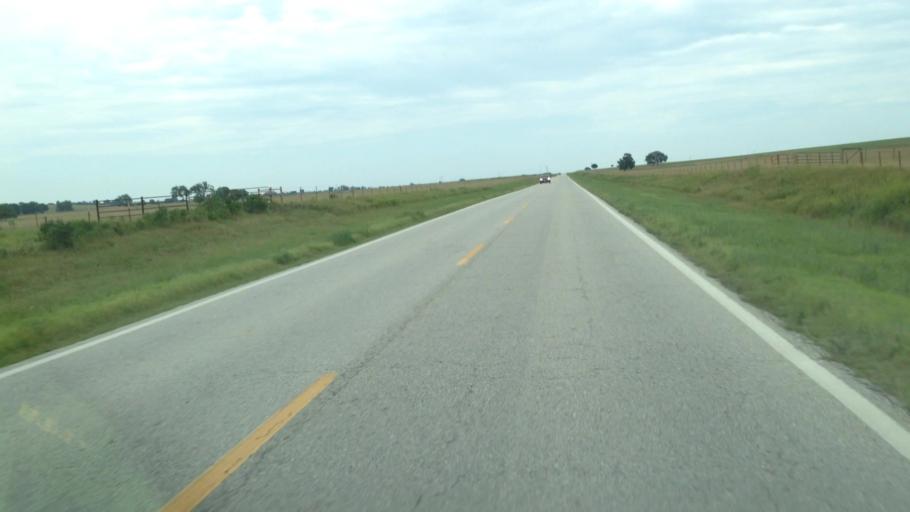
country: US
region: Oklahoma
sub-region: Craig County
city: Vinita
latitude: 36.8368
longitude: -95.1315
